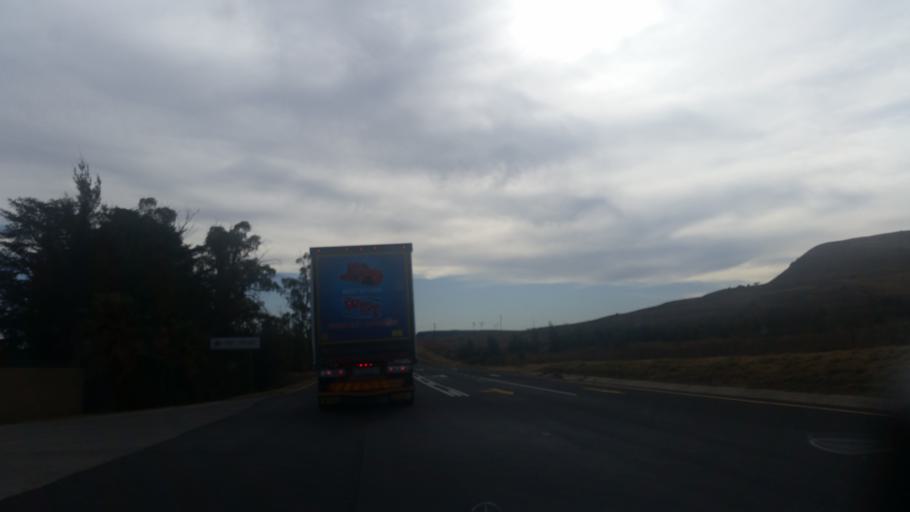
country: ZA
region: Orange Free State
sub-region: Thabo Mofutsanyana District Municipality
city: Phuthaditjhaba
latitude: -28.3132
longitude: 28.7284
